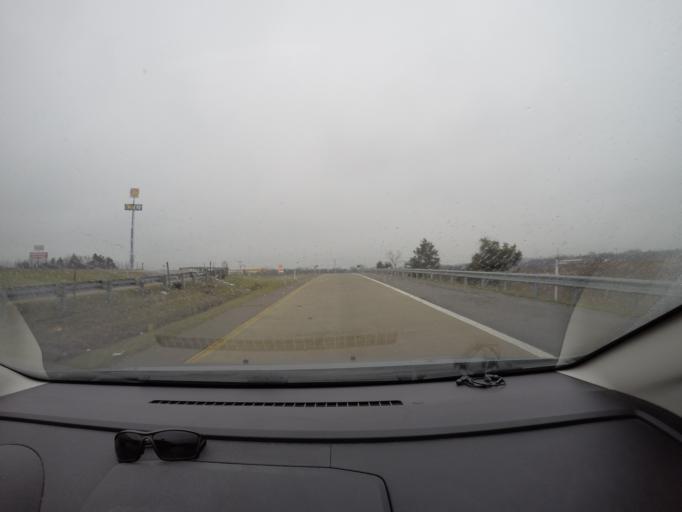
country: US
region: Tennessee
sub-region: Rutherford County
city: Plainview
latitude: 35.7221
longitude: -86.3223
